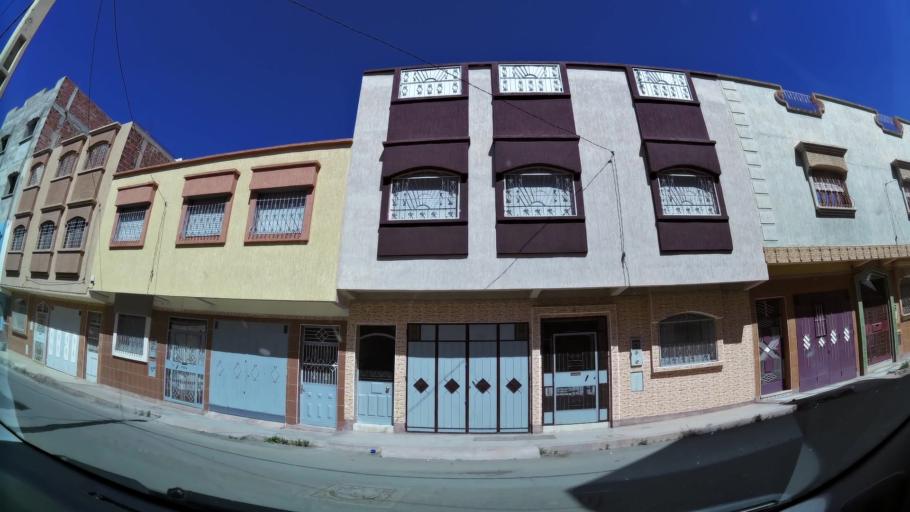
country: MA
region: Oriental
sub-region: Oujda-Angad
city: Oujda
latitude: 34.6827
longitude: -1.9410
